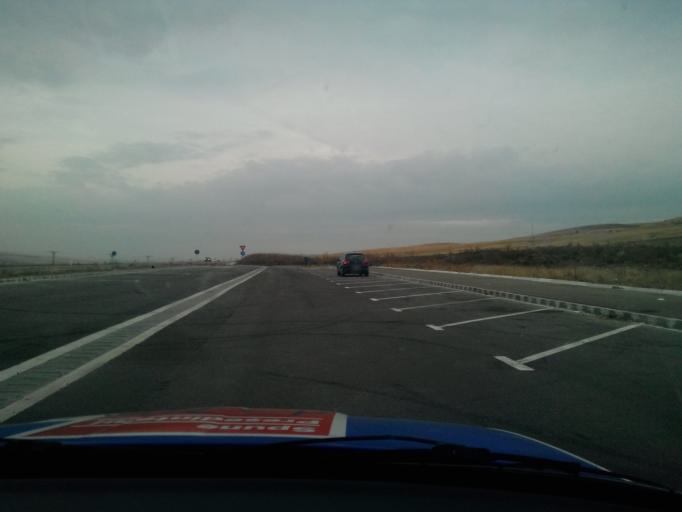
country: RO
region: Vaslui
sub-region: Comuna Albesti
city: Corni-Albesti
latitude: 46.5307
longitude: 27.8373
